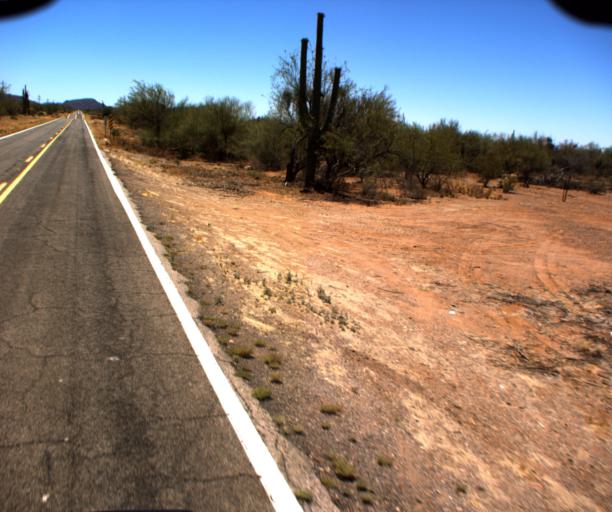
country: US
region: Arizona
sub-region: Pima County
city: Sells
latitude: 32.0089
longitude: -111.9924
